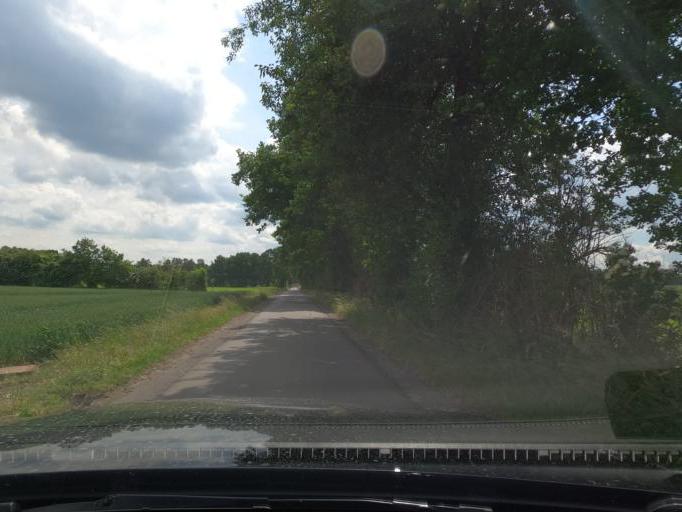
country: DE
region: Lower Saxony
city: Steimbke
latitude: 52.6326
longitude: 9.4252
